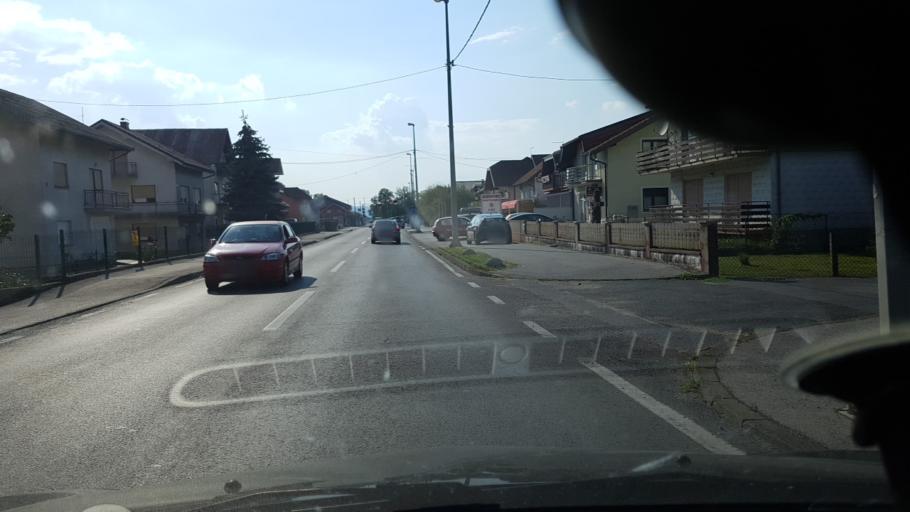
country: HR
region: Zagrebacka
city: Brdovec
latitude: 45.8624
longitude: 15.7925
